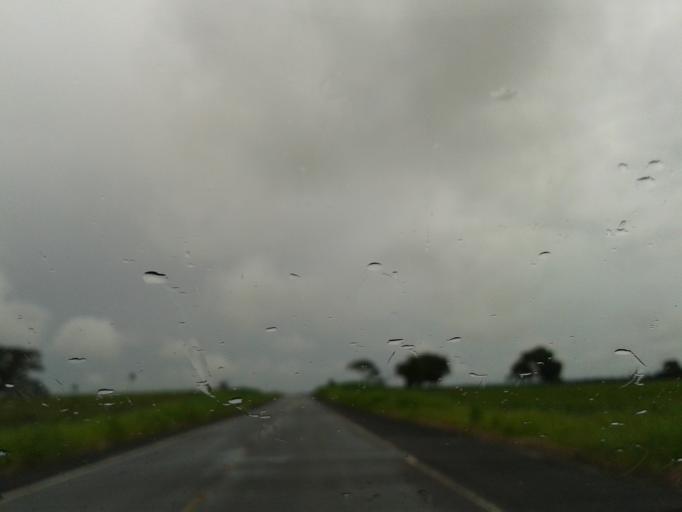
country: BR
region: Minas Gerais
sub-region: Santa Vitoria
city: Santa Vitoria
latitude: -19.1549
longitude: -50.1328
